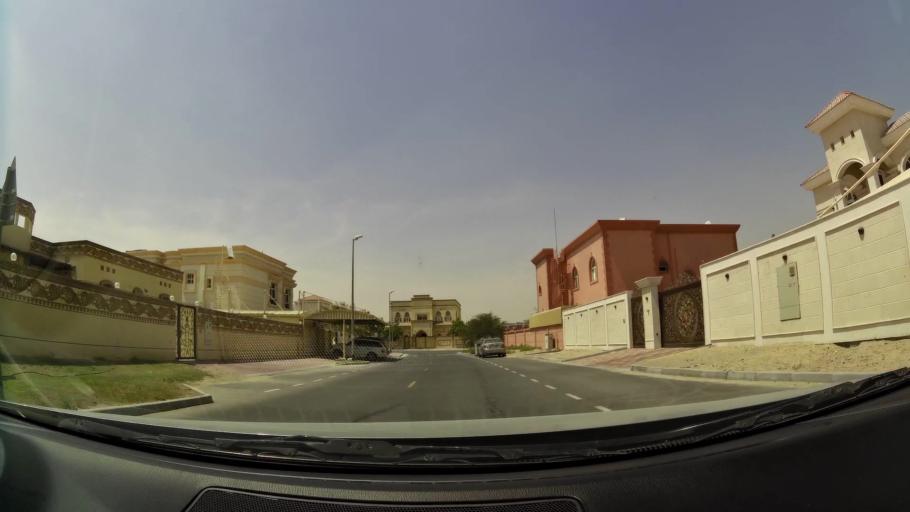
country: AE
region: Ash Shariqah
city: Sharjah
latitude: 25.1794
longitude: 55.4148
